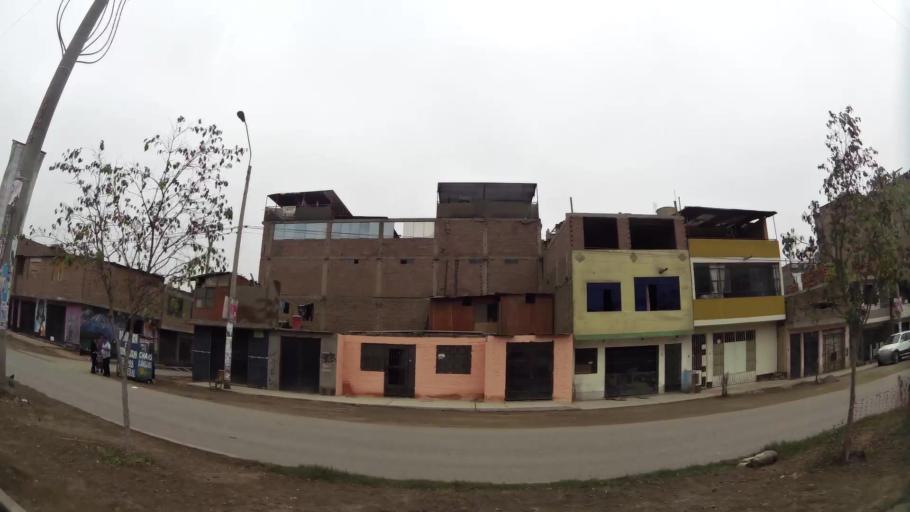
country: PE
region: Lima
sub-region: Lima
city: Independencia
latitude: -11.9422
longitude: -76.9840
